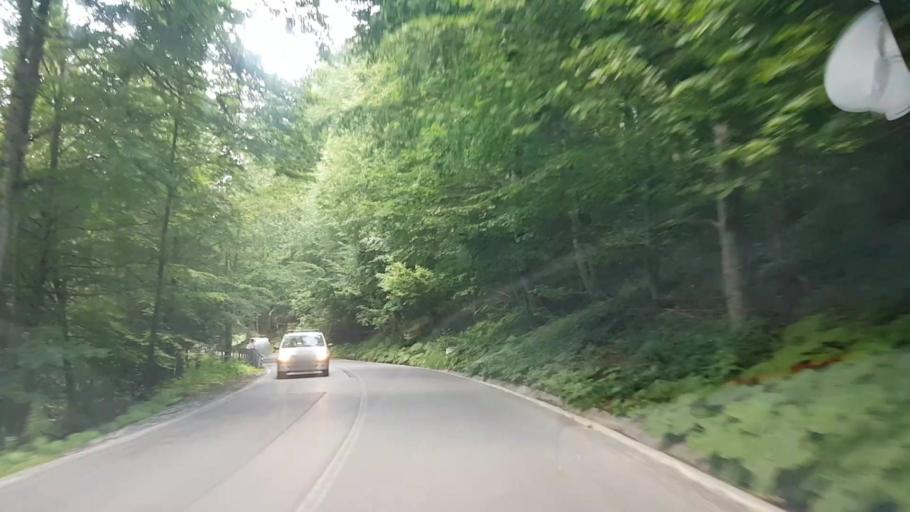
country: RO
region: Harghita
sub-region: Comuna Praid
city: Ocna de Sus
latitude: 46.6172
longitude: 25.2473
